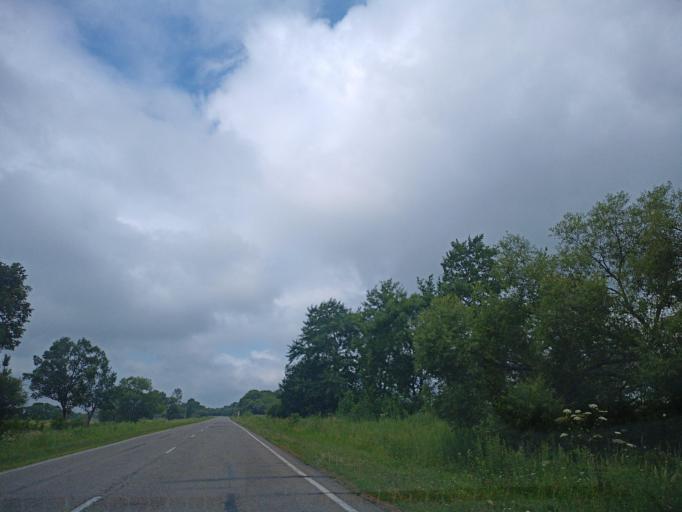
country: RU
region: Primorskiy
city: Dal'nerechensk
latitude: 45.9469
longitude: 133.8934
